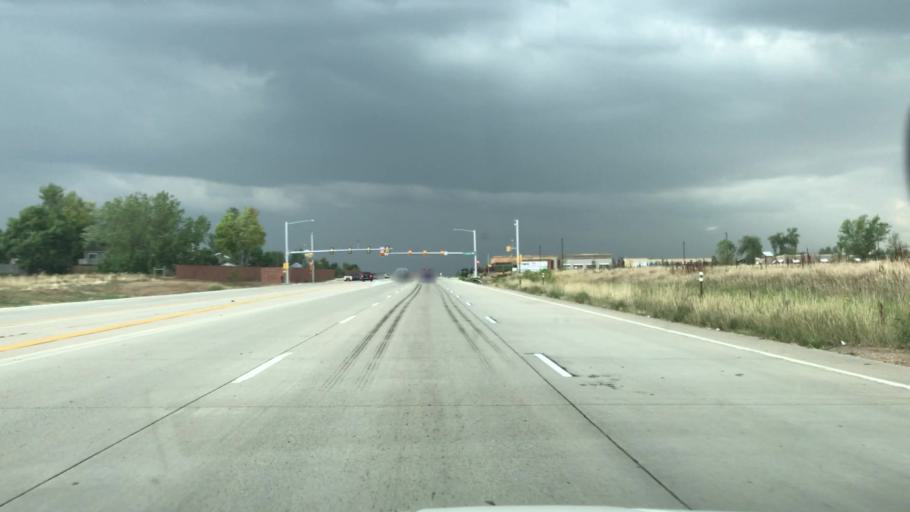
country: US
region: Colorado
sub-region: Boulder County
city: Lafayette
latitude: 40.0121
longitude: -105.1030
